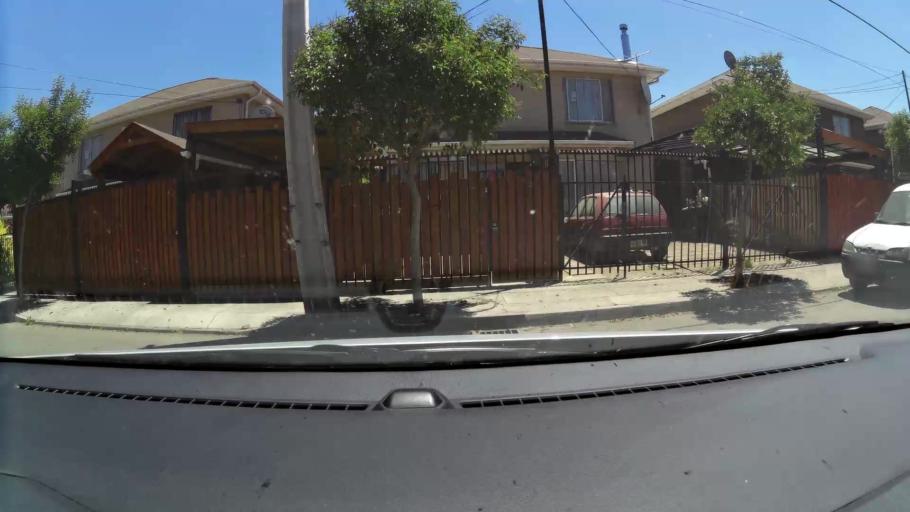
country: CL
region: Santiago Metropolitan
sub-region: Provincia de Maipo
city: San Bernardo
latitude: -33.6033
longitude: -70.6745
